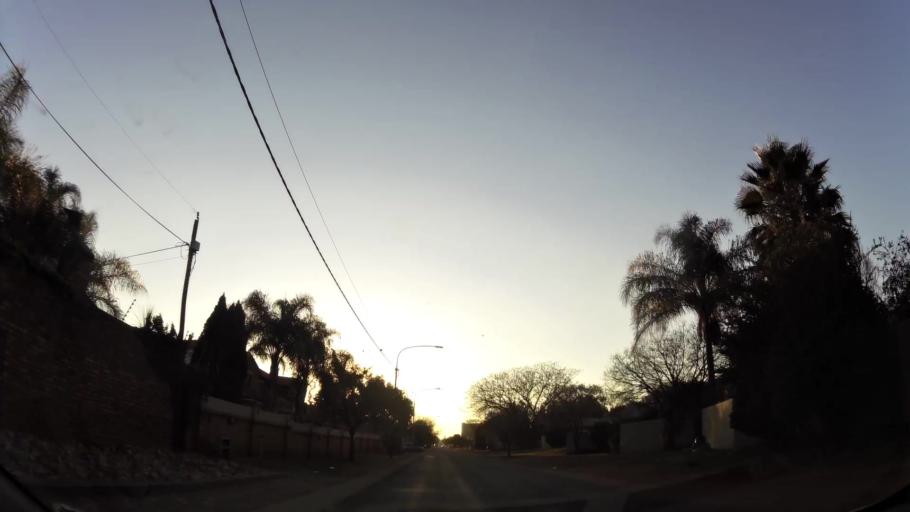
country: ZA
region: Gauteng
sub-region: City of Tshwane Metropolitan Municipality
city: Centurion
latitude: -25.8547
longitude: 28.1979
